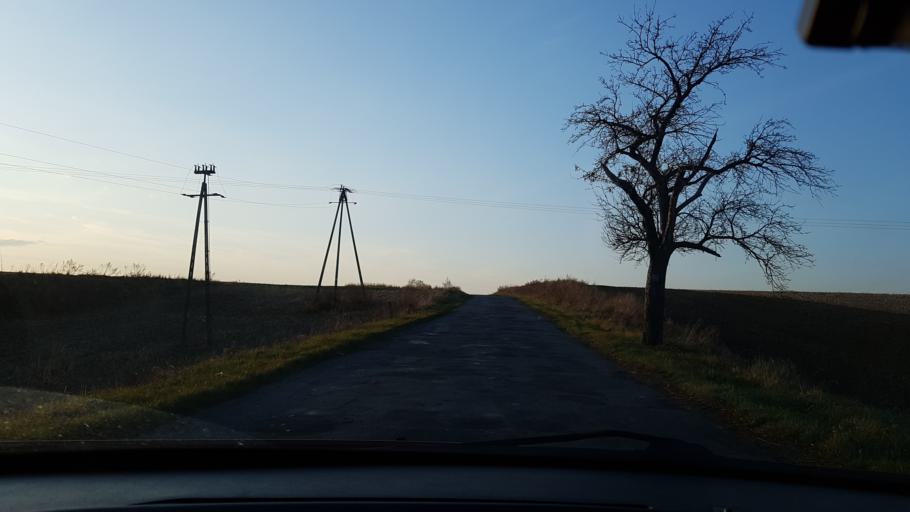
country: PL
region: Lower Silesian Voivodeship
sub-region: Powiat zabkowicki
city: Henrykow
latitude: 50.6586
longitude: 17.0079
